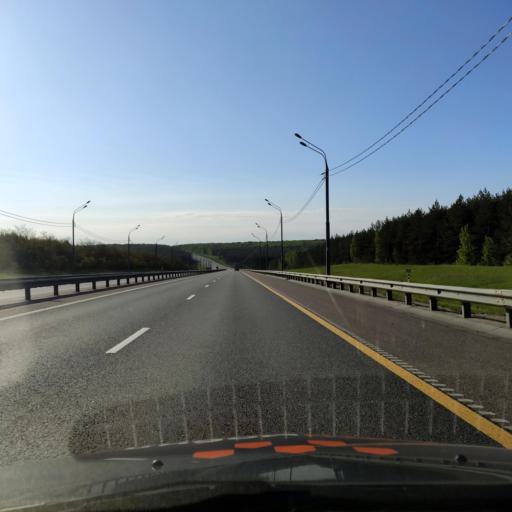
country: RU
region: Lipetsk
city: Khlevnoye
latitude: 52.2290
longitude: 39.0950
